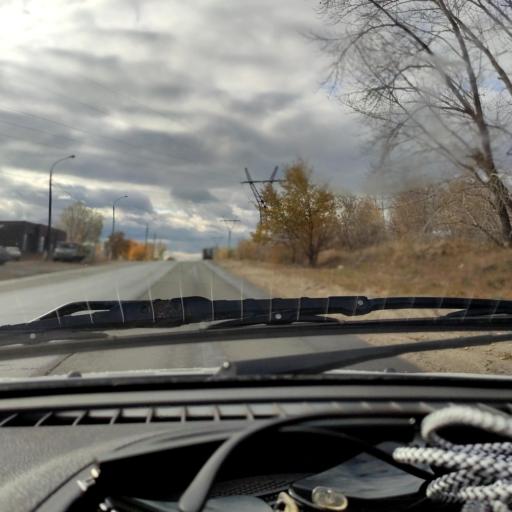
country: RU
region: Samara
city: Zhigulevsk
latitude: 53.4815
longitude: 49.5017
